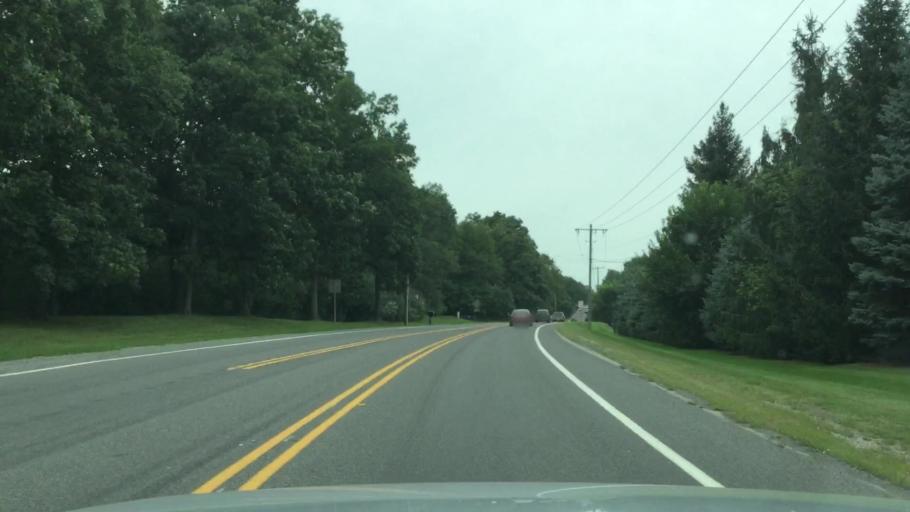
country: US
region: Michigan
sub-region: Washtenaw County
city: Ypsilanti
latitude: 42.2014
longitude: -83.6604
